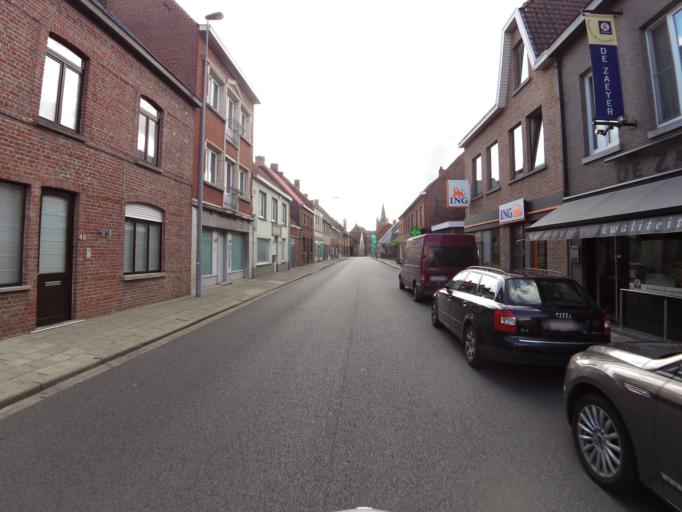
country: BE
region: Flanders
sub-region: Provincie West-Vlaanderen
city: Oostkamp
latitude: 51.0973
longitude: 3.2101
